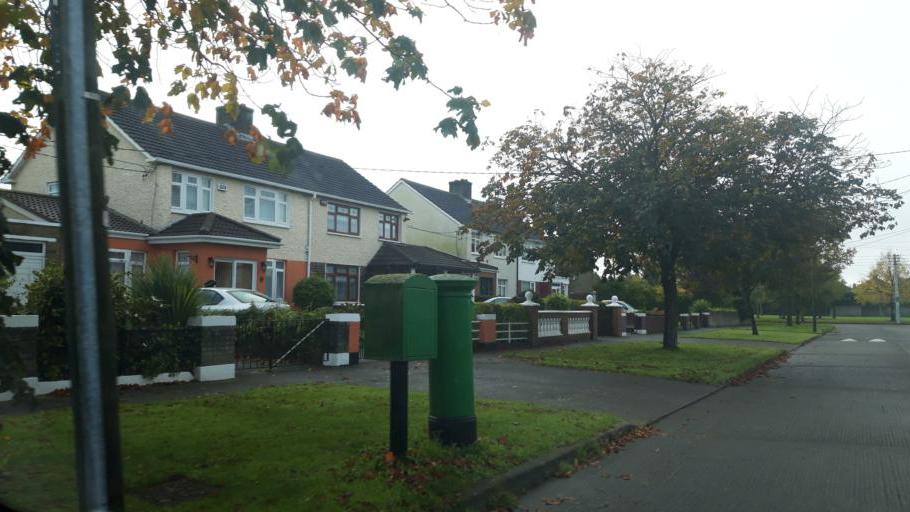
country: IE
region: Leinster
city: Artane
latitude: 53.3902
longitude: -6.2086
